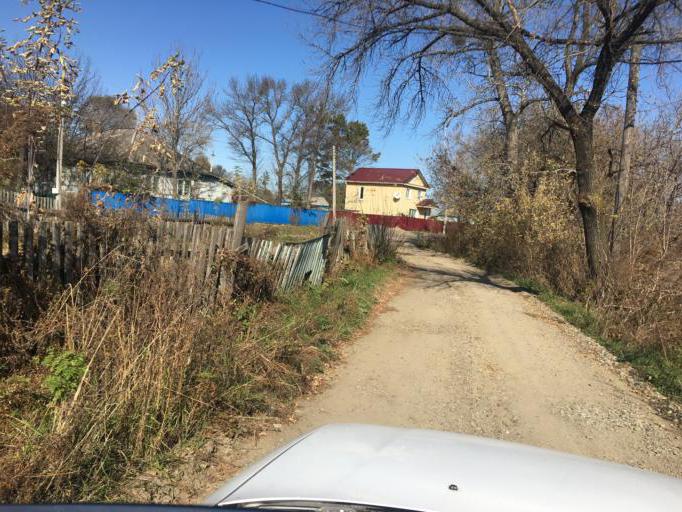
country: RU
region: Primorskiy
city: Dal'nerechensk
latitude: 45.9096
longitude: 133.7954
